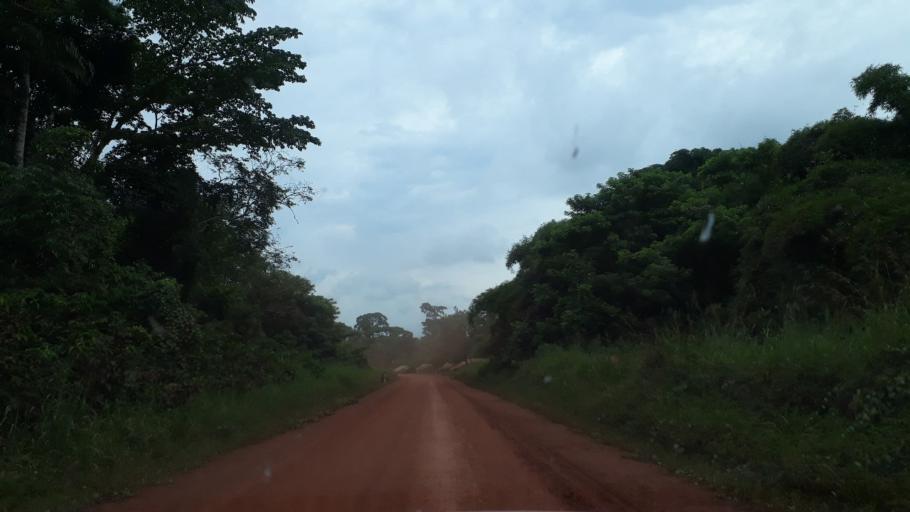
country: CD
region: Eastern Province
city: Kisangani
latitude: 0.5995
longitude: 25.9750
